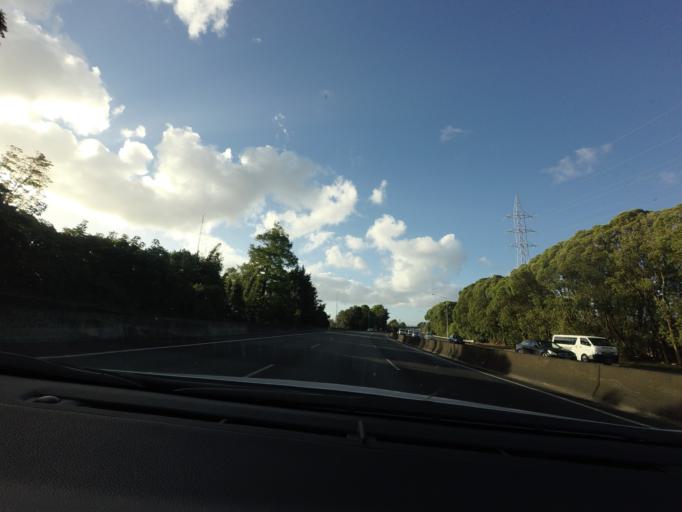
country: NZ
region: Auckland
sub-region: Auckland
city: Manukau City
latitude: -36.9606
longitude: 174.8632
